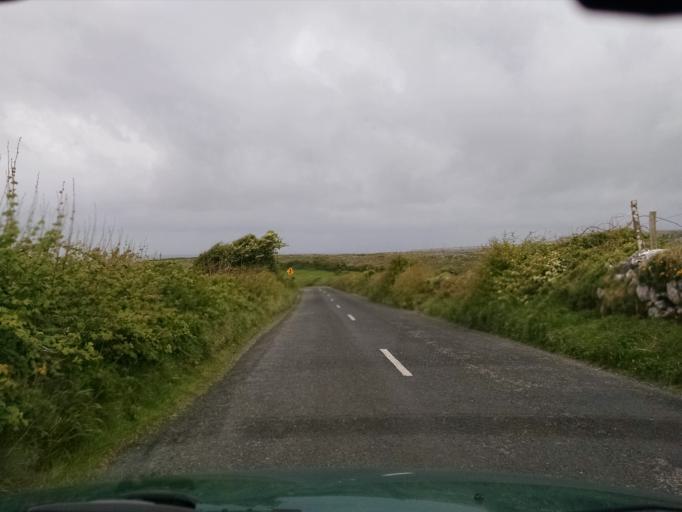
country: IE
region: Connaught
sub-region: County Galway
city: Bearna
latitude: 53.0538
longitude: -9.3485
